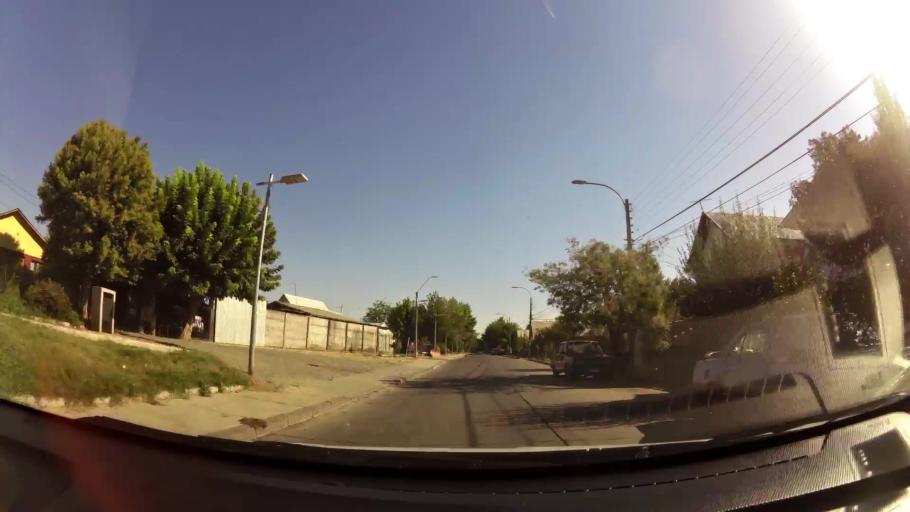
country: CL
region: Maule
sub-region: Provincia de Curico
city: Curico
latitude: -34.9992
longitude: -71.2458
